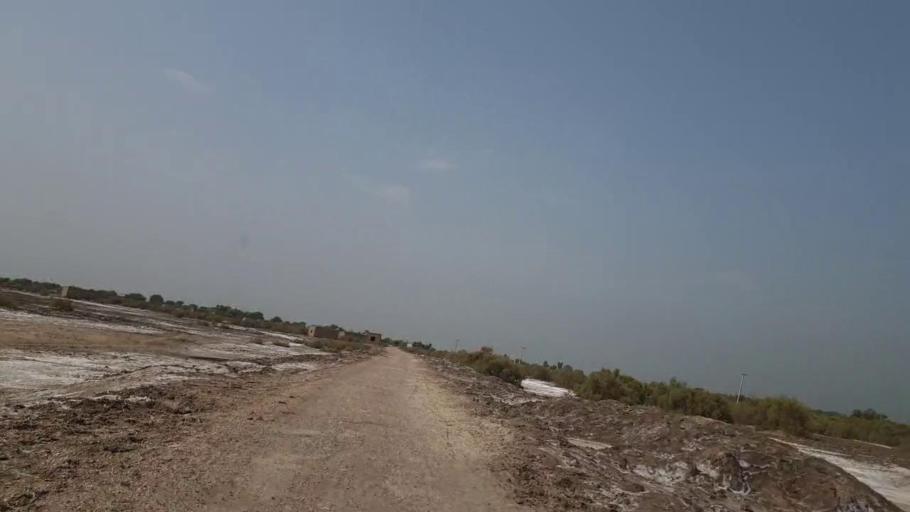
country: PK
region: Sindh
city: Dokri
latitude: 27.4194
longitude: 68.2055
